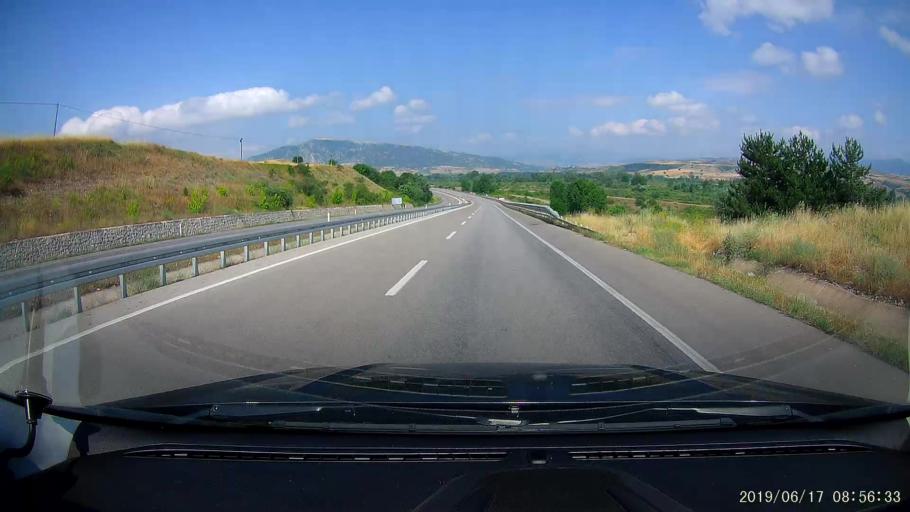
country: TR
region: Amasya
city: Esencay
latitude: 40.7345
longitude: 36.4187
